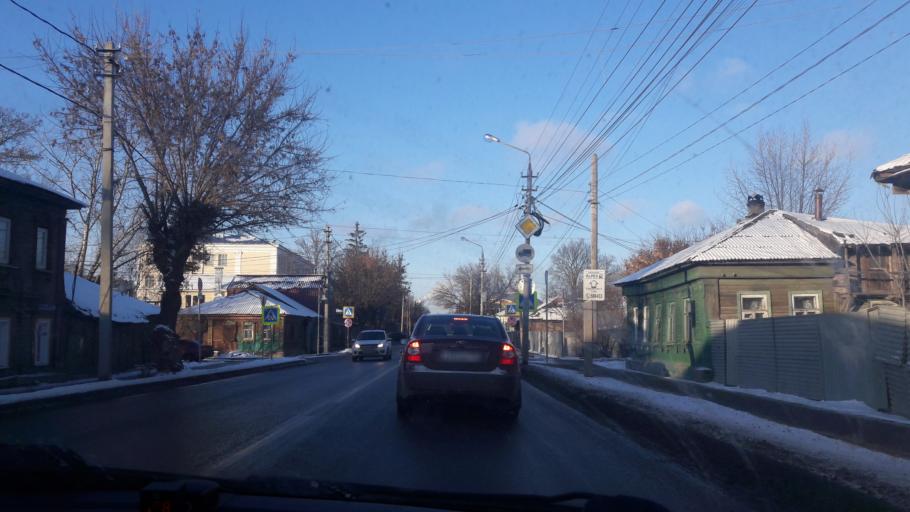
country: RU
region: Tula
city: Tula
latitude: 54.1853
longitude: 37.6272
